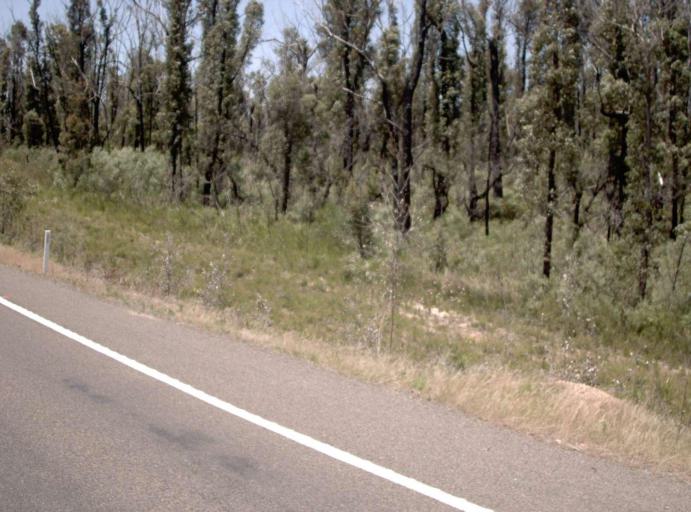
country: AU
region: Victoria
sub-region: East Gippsland
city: Lakes Entrance
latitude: -37.7496
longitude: 148.2219
